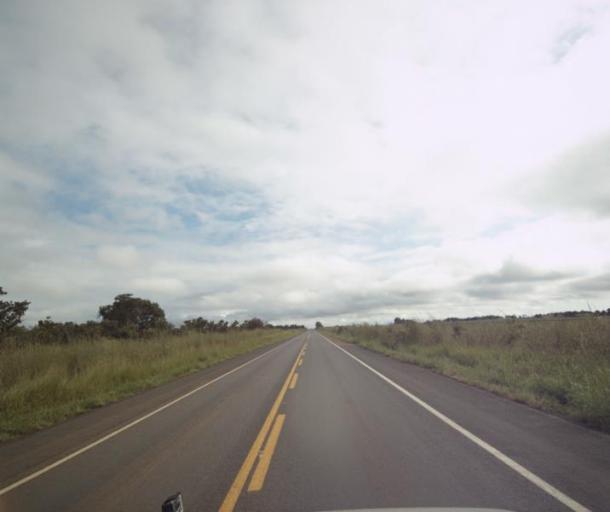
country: BR
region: Goias
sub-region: Padre Bernardo
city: Padre Bernardo
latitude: -15.3639
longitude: -48.6461
